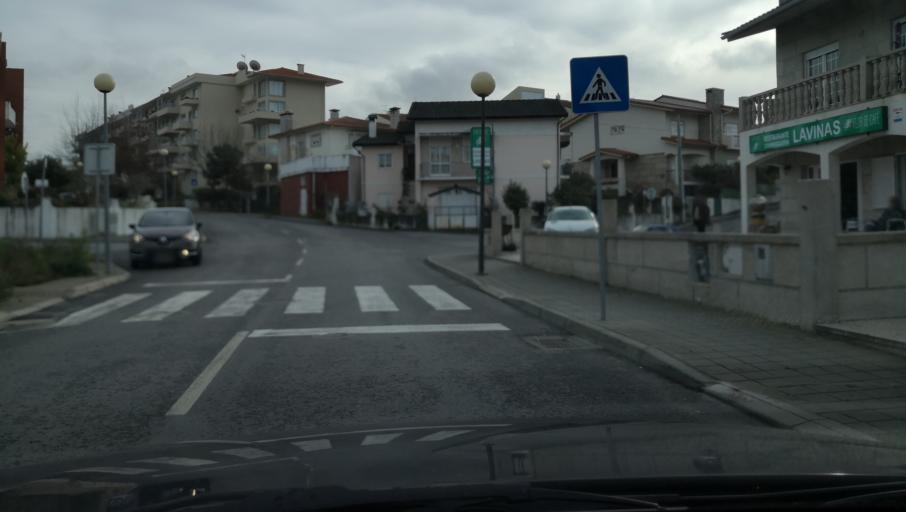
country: PT
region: Vila Real
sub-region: Vila Real
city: Vila Real
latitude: 41.2935
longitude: -7.7272
